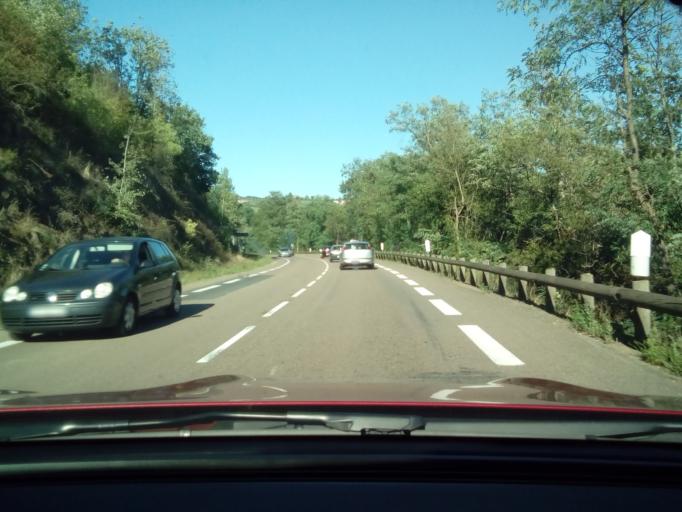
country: FR
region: Rhone-Alpes
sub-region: Departement du Rhone
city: Saint-Verand
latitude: 45.9025
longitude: 4.5653
